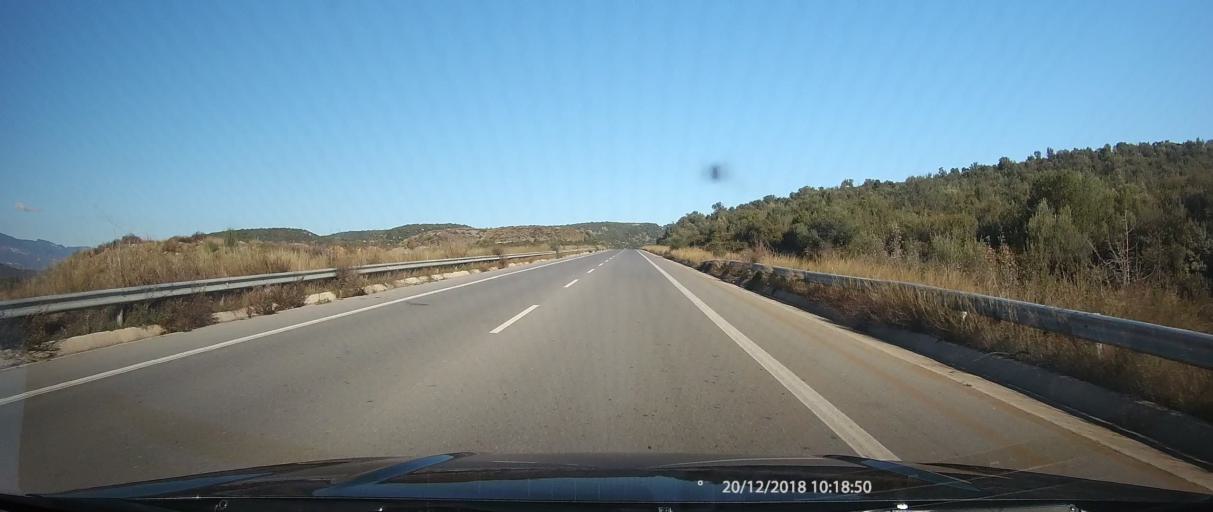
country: GR
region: Peloponnese
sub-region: Nomos Lakonias
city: Magoula
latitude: 37.1235
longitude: 22.4204
